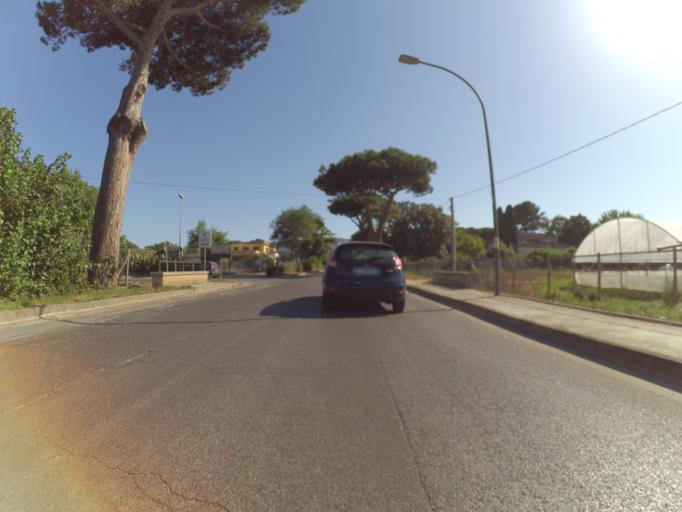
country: IT
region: Latium
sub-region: Provincia di Latina
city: San Felice Circeo
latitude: 41.2609
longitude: 13.0922
